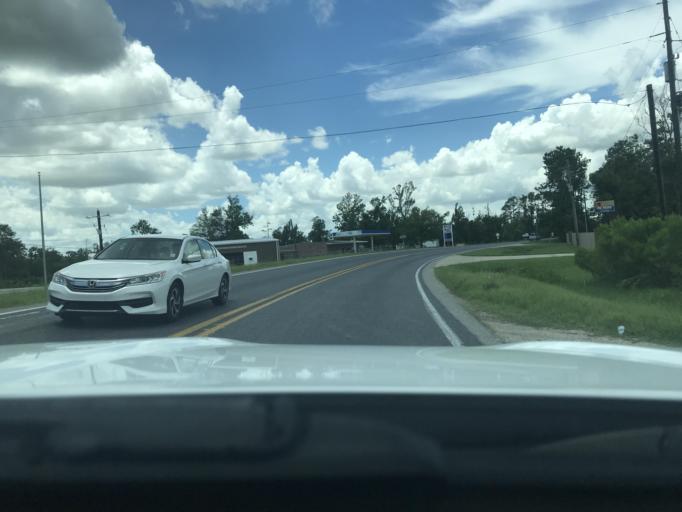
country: US
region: Louisiana
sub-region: Calcasieu Parish
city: Moss Bluff
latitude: 30.2774
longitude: -93.1692
